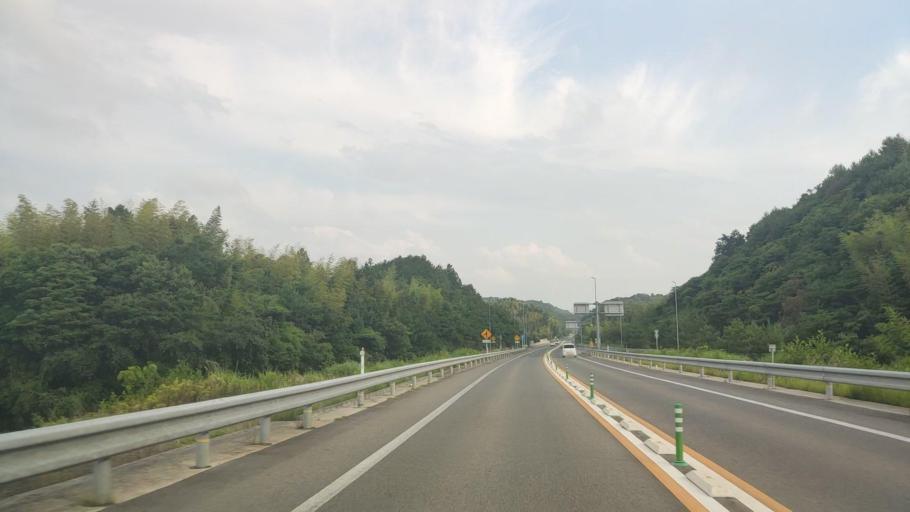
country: JP
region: Tottori
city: Kurayoshi
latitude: 35.4653
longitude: 133.8086
